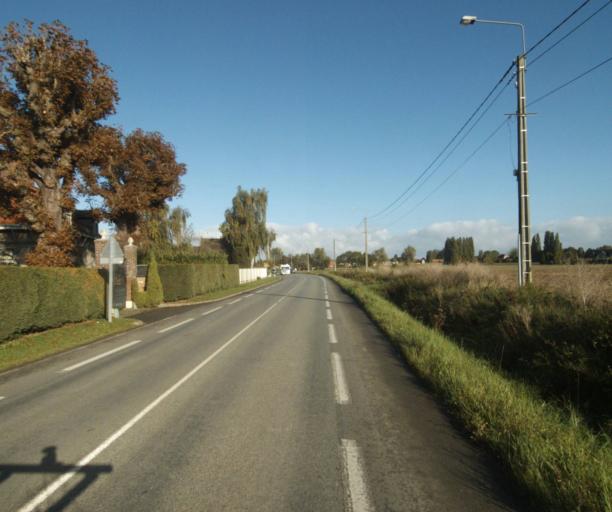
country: FR
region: Nord-Pas-de-Calais
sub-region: Departement du Nord
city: Verlinghem
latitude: 50.6741
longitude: 3.0021
